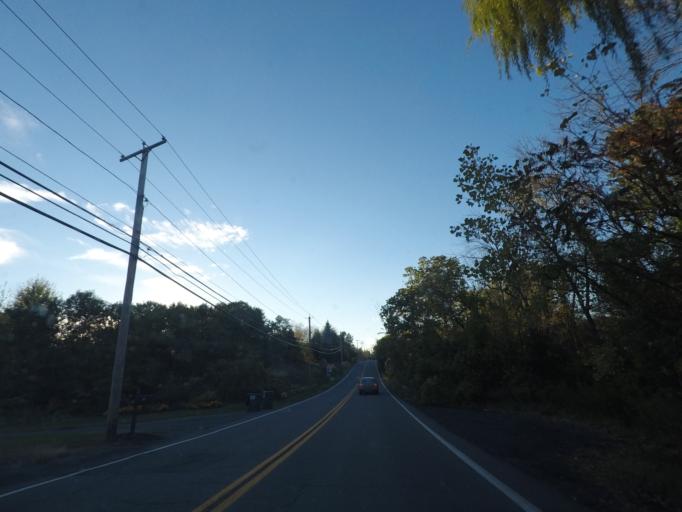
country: US
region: New York
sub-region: Albany County
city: Watervliet
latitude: 42.7473
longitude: -73.7206
